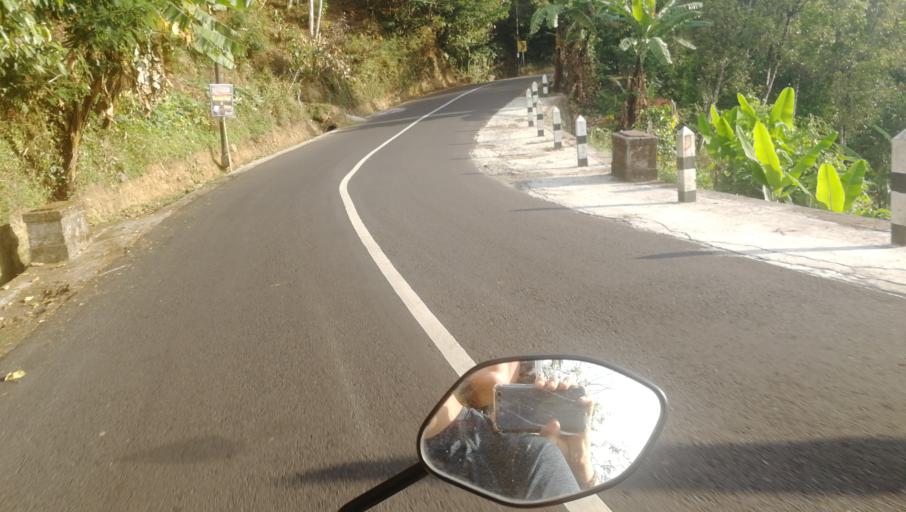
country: ID
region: Bali
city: Munduk
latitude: -8.2576
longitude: 115.0723
